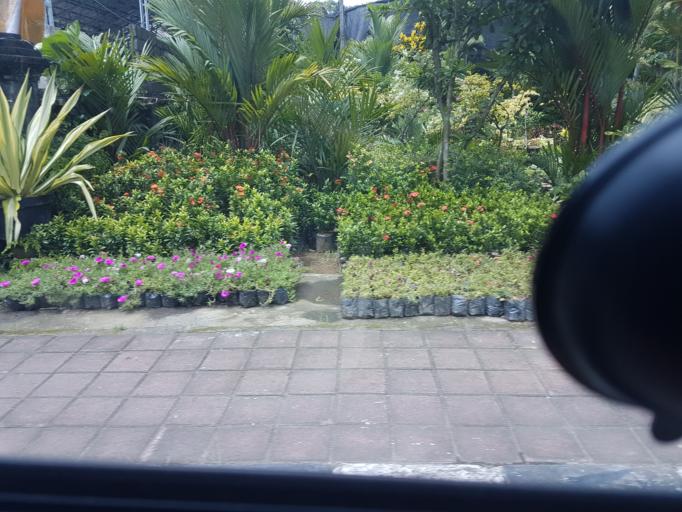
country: ID
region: Bali
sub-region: Kabupaten Gianyar
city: Ubud
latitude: -8.5352
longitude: 115.2725
